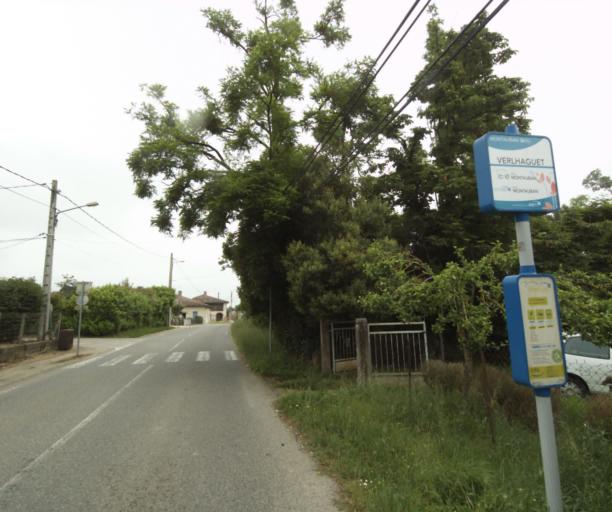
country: FR
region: Midi-Pyrenees
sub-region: Departement du Tarn-et-Garonne
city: Montbeton
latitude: 43.9879
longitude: 1.3114
